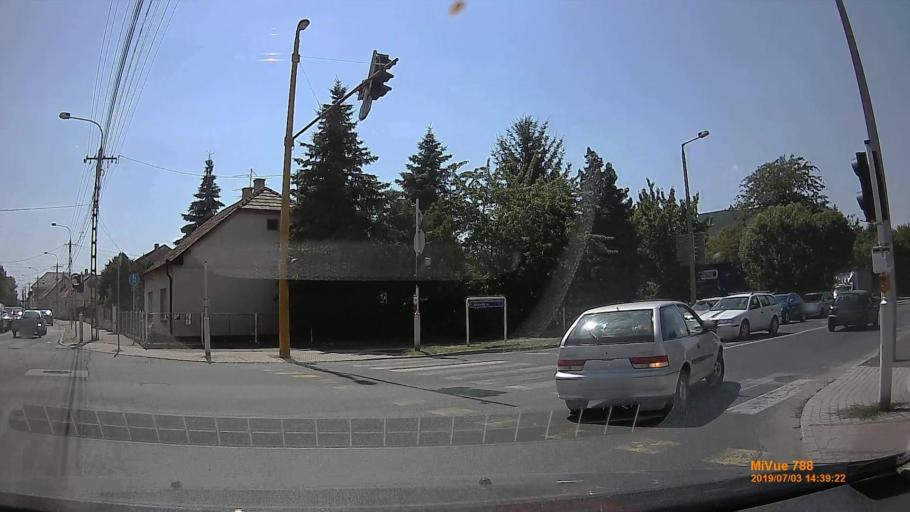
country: HU
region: Gyor-Moson-Sopron
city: Gyor
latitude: 47.6650
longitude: 17.6632
